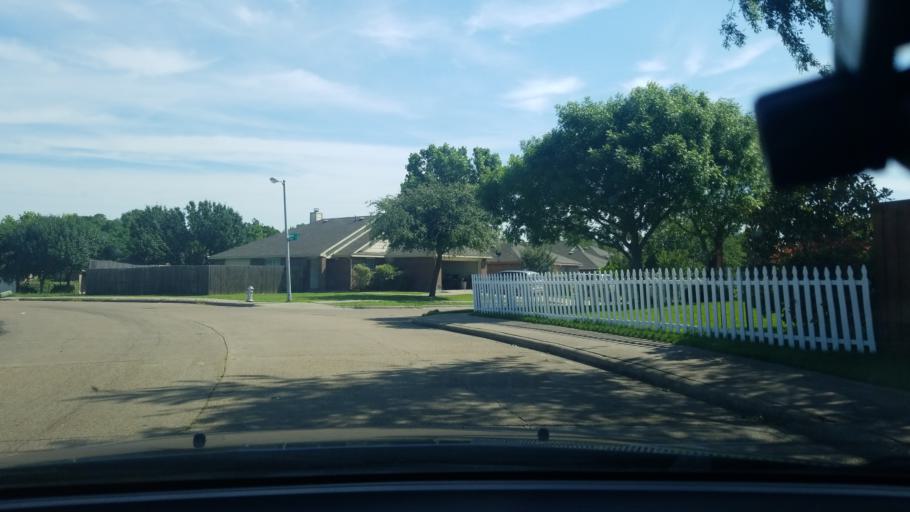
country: US
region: Texas
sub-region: Dallas County
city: Mesquite
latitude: 32.7788
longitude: -96.5956
